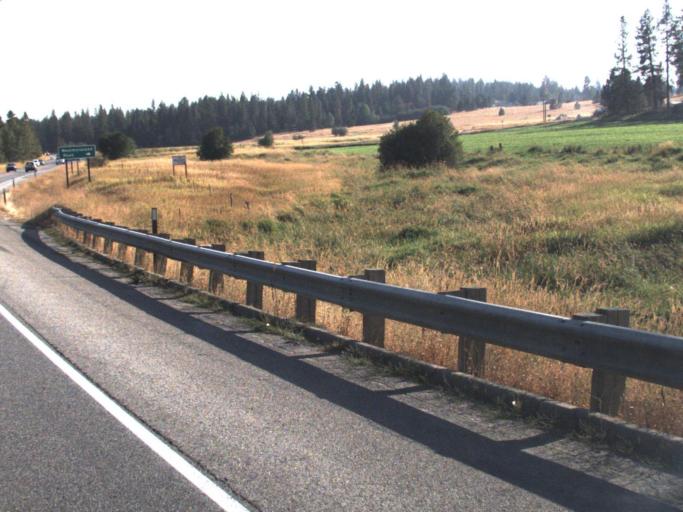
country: US
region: Washington
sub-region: Spokane County
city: Deer Park
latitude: 47.9425
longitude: -117.3504
